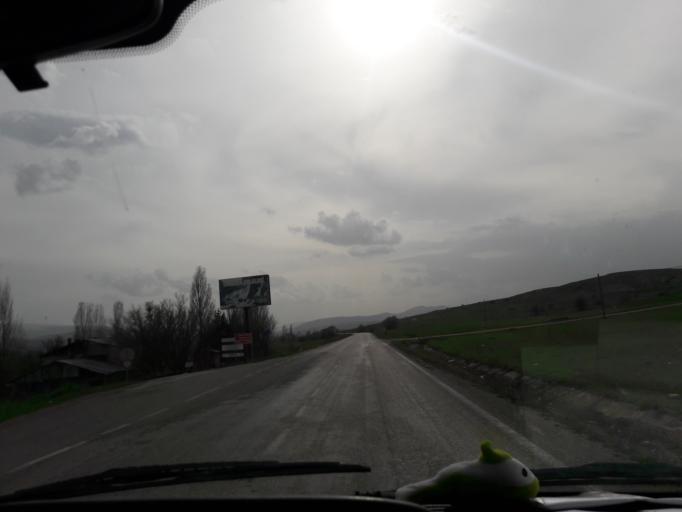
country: TR
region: Gumushane
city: Siran
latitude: 40.1715
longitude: 39.0762
